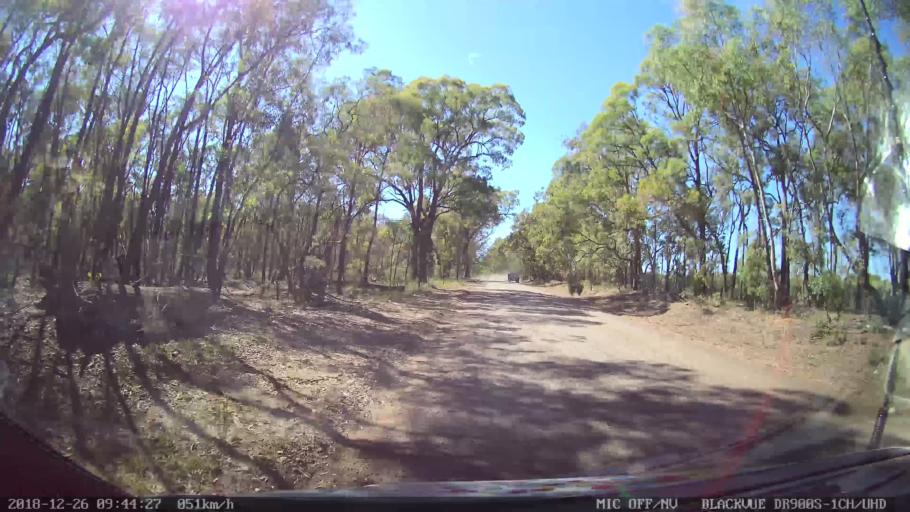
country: AU
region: New South Wales
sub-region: Mid-Western Regional
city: Kandos
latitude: -32.9570
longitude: 150.0969
